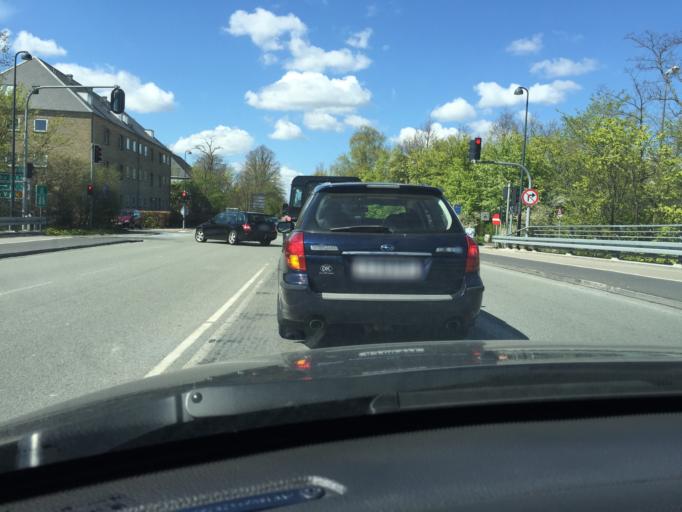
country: DK
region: Capital Region
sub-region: Lyngby-Tarbaek Kommune
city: Kongens Lyngby
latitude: 55.7646
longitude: 12.5214
